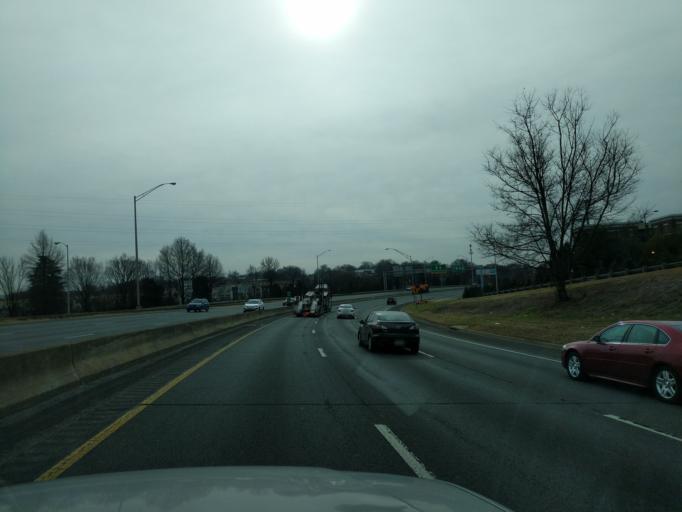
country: US
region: North Carolina
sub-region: Mecklenburg County
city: Charlotte
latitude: 35.2278
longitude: -80.8290
